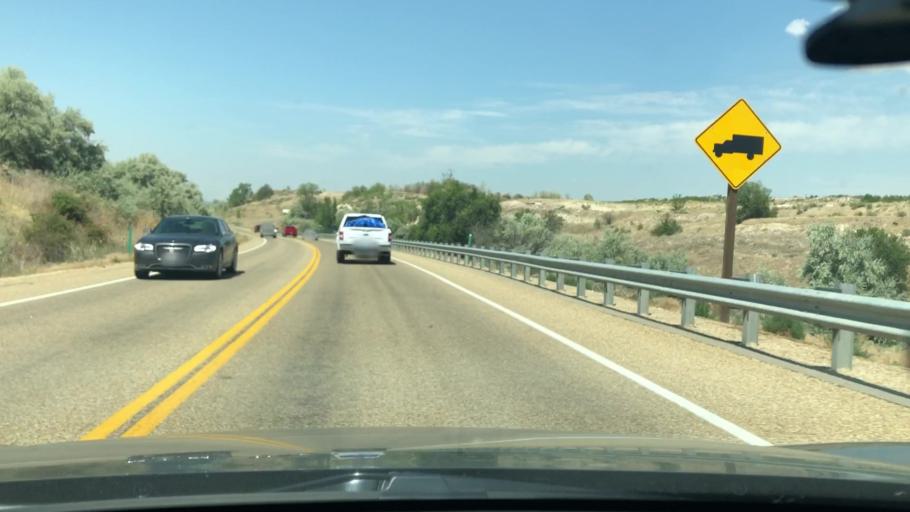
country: US
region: Idaho
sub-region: Canyon County
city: Wilder
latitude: 43.7172
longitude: -116.9118
